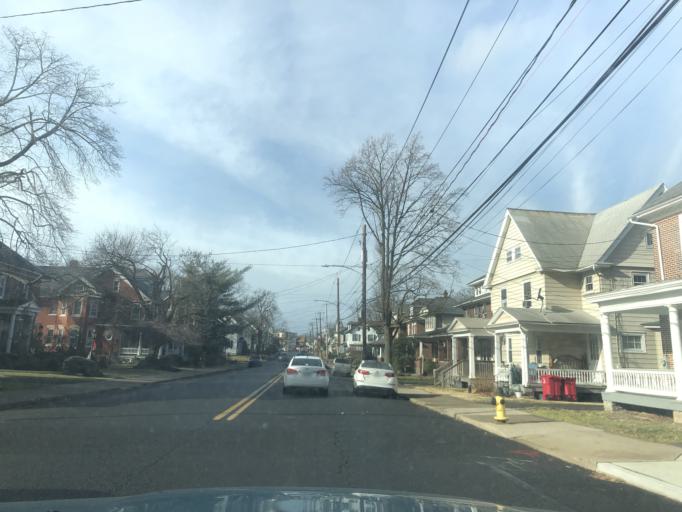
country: US
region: Pennsylvania
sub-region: Bucks County
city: Quakertown
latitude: 40.4424
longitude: -75.3489
